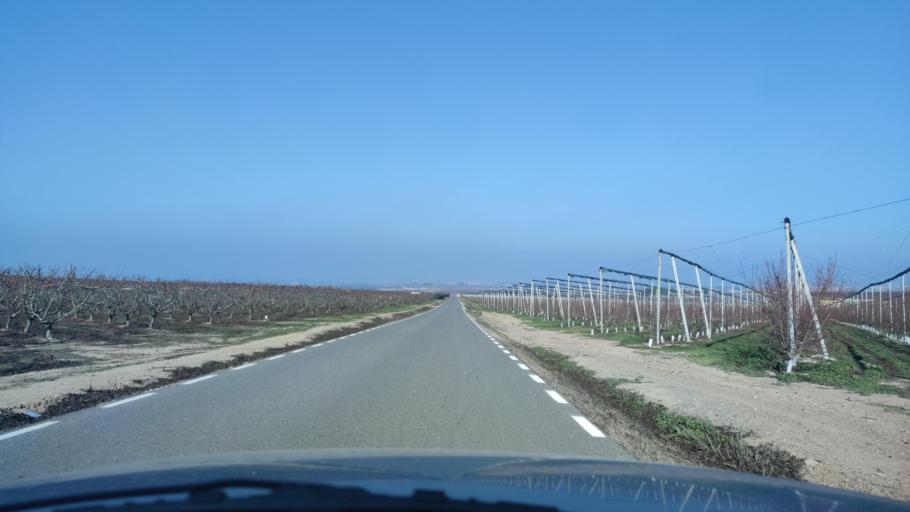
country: ES
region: Catalonia
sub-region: Provincia de Lleida
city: Sunyer
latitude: 41.5257
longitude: 0.5722
